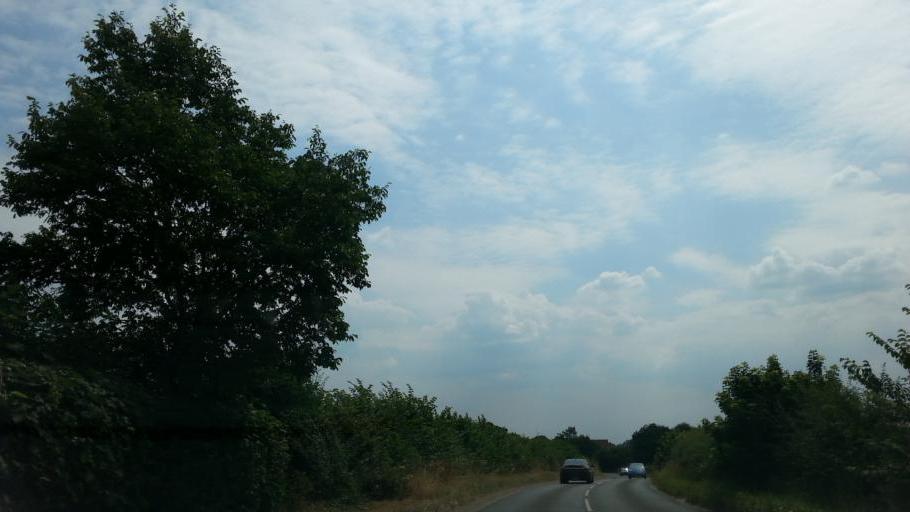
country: GB
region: England
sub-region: Suffolk
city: Lakenheath
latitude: 52.4021
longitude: 0.5286
